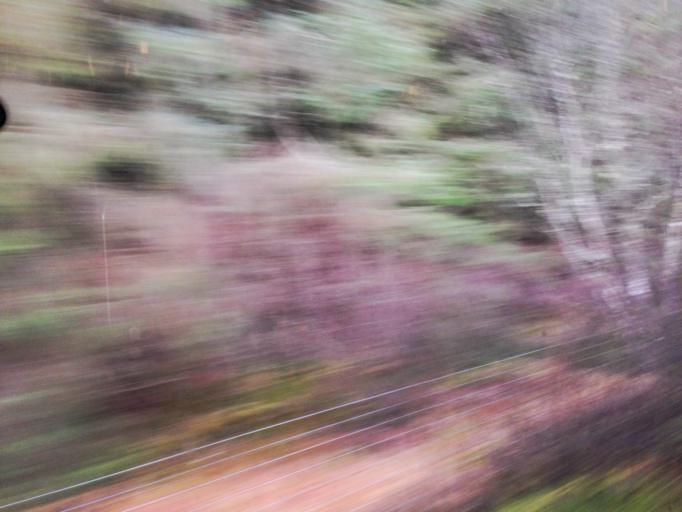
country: GB
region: Scotland
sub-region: Highland
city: Fort William
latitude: 56.8455
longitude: -5.1559
